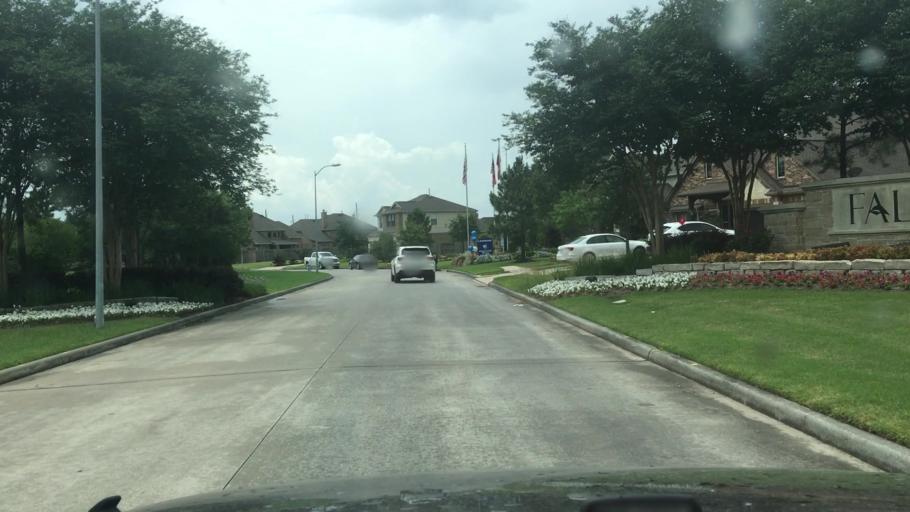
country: US
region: Texas
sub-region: Harris County
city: Humble
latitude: 29.9318
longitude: -95.2462
